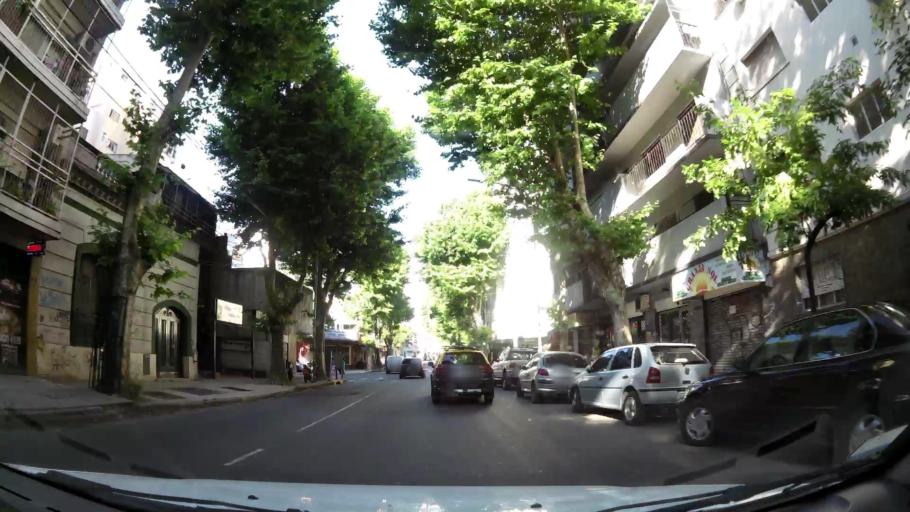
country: AR
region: Buenos Aires F.D.
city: Villa Santa Rita
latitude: -34.6165
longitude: -58.4436
